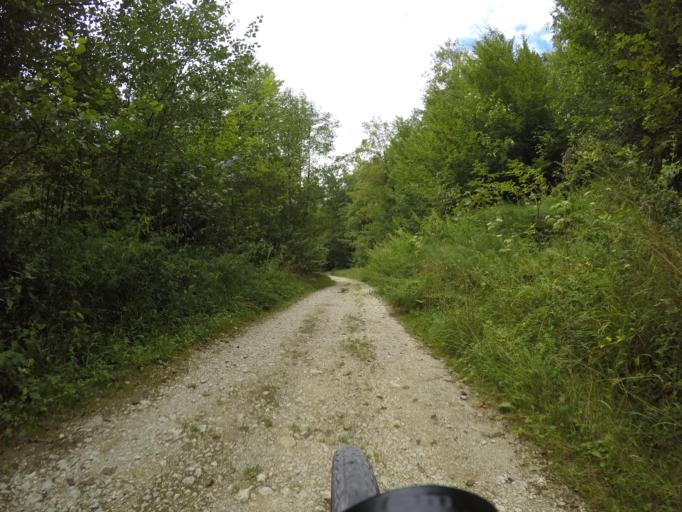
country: DE
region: Baden-Wuerttemberg
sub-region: Tuebingen Region
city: Reutlingen
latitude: 48.4560
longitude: 9.1711
